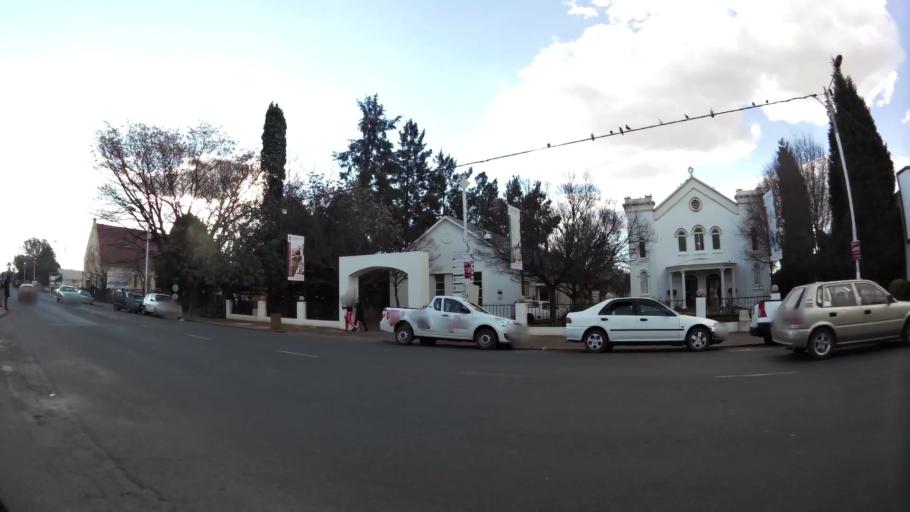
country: ZA
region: North-West
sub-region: Dr Kenneth Kaunda District Municipality
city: Potchefstroom
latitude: -26.7109
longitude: 27.0963
